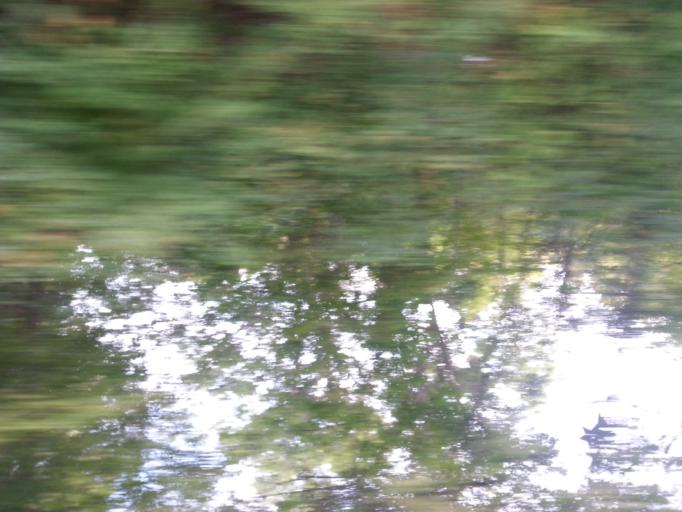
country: US
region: Tennessee
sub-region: Knox County
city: Knoxville
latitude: 35.9158
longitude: -83.8990
